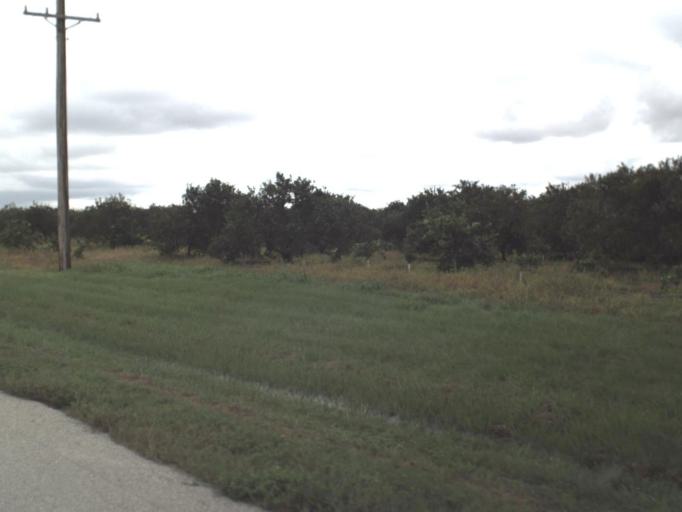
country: US
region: Florida
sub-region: Hillsborough County
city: Balm
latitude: 27.5913
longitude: -82.0853
